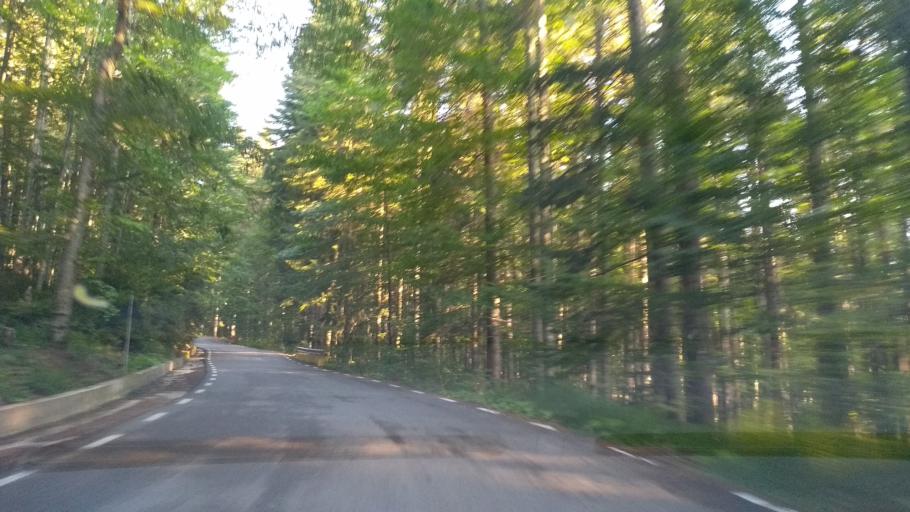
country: RO
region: Prahova
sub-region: Oras Sinaia
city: Sinaia
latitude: 45.3154
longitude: 25.5195
